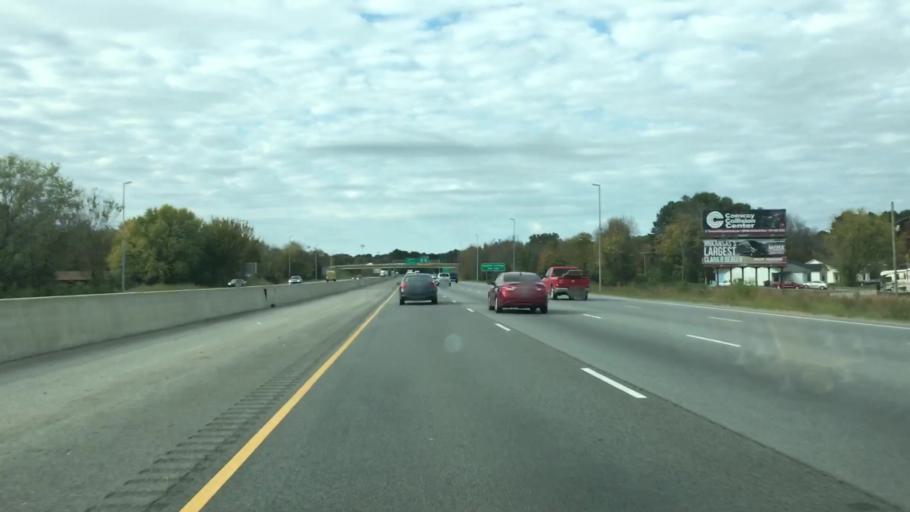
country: US
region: Arkansas
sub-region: Faulkner County
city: Conway
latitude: 35.0958
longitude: -92.4268
